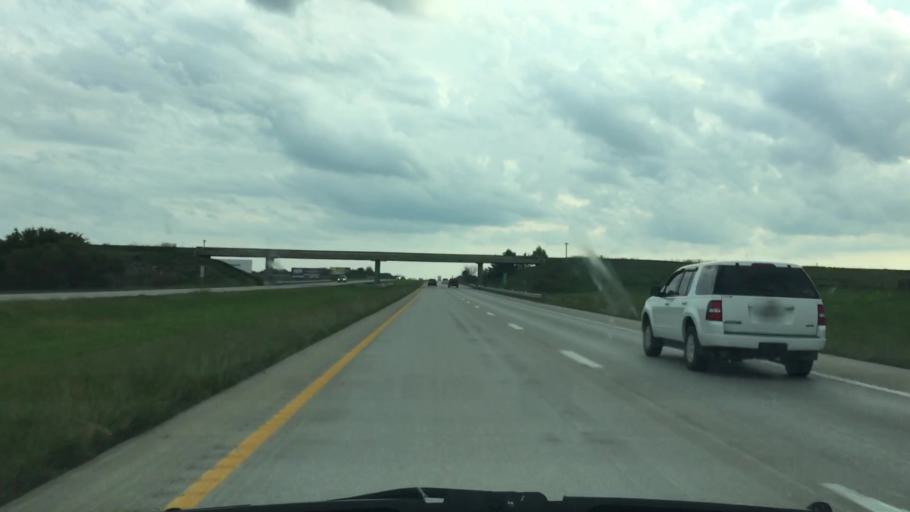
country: US
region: Missouri
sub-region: Clinton County
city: Cameron
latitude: 39.6344
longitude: -94.2442
